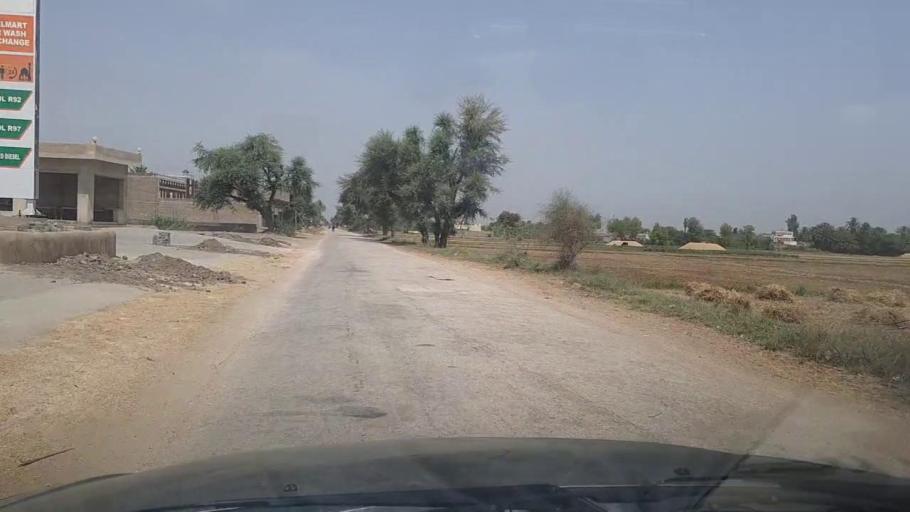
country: PK
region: Sindh
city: Setharja Old
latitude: 27.1933
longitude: 68.4914
